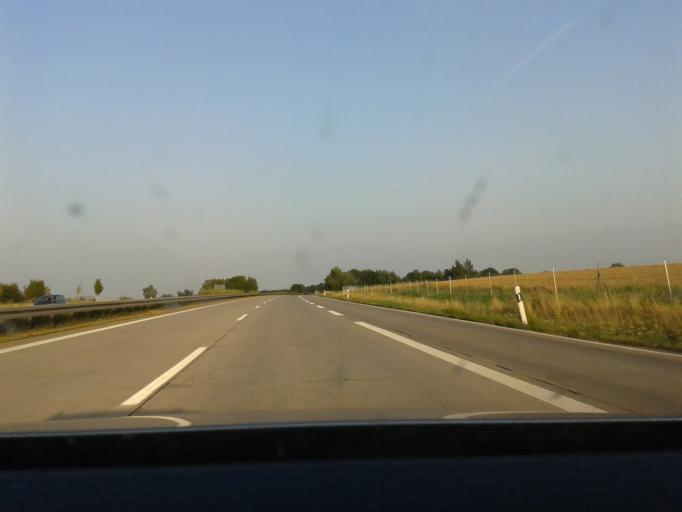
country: DE
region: Saxony
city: Grossweitzschen
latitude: 51.1881
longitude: 13.0112
